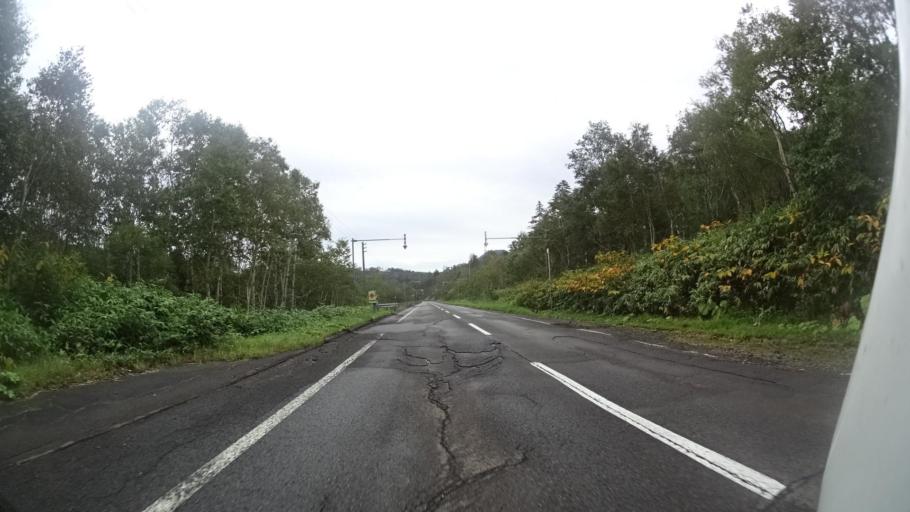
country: JP
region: Hokkaido
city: Shibetsu
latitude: 43.7572
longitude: 144.8080
